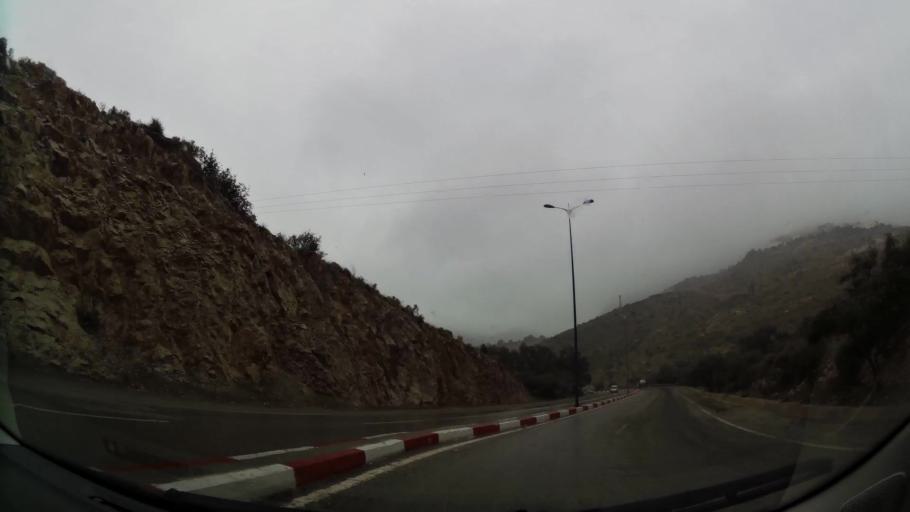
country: MA
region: Taza-Al Hoceima-Taounate
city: Al Hoceima
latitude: 35.2199
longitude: -3.9207
